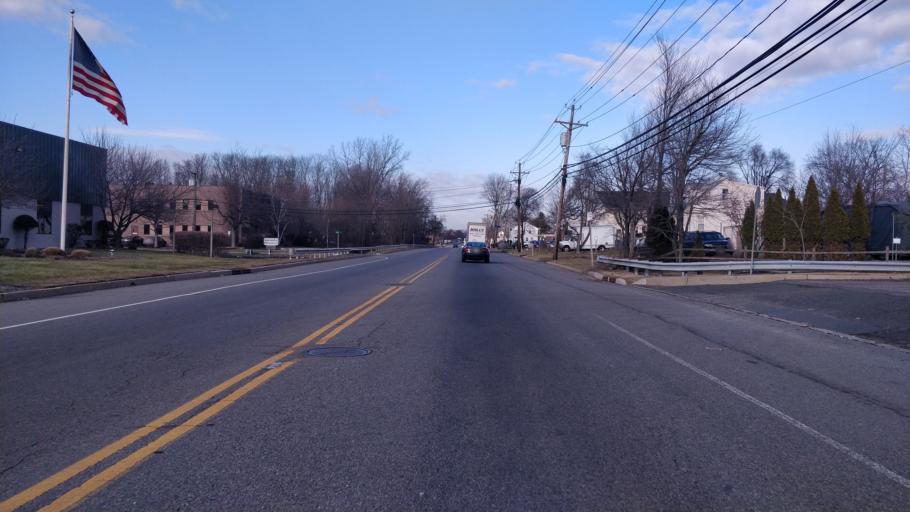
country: US
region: New Jersey
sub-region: Middlesex County
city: South Plainfield
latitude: 40.5713
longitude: -74.4303
